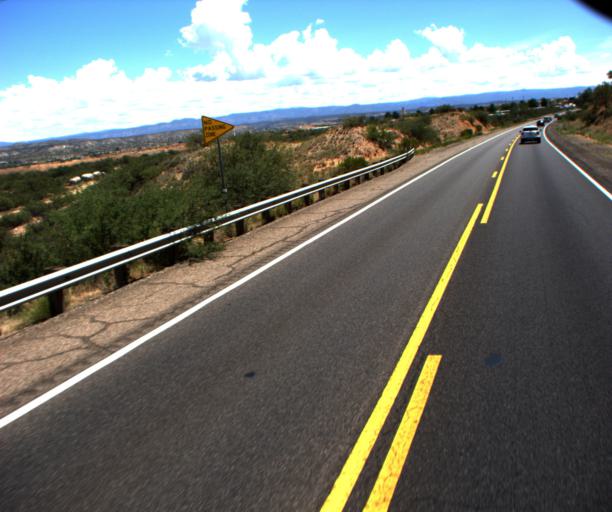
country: US
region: Arizona
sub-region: Yavapai County
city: Camp Verde
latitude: 34.6213
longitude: -111.9238
